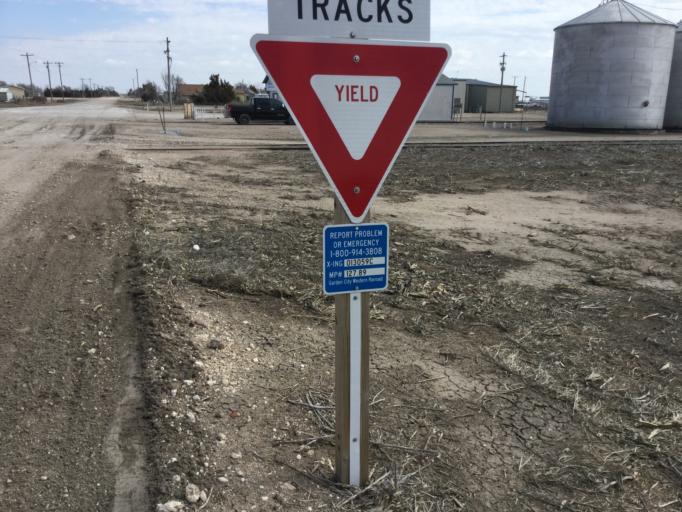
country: US
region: Kansas
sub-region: Scott County
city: Scott City
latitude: 38.3737
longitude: -100.9153
